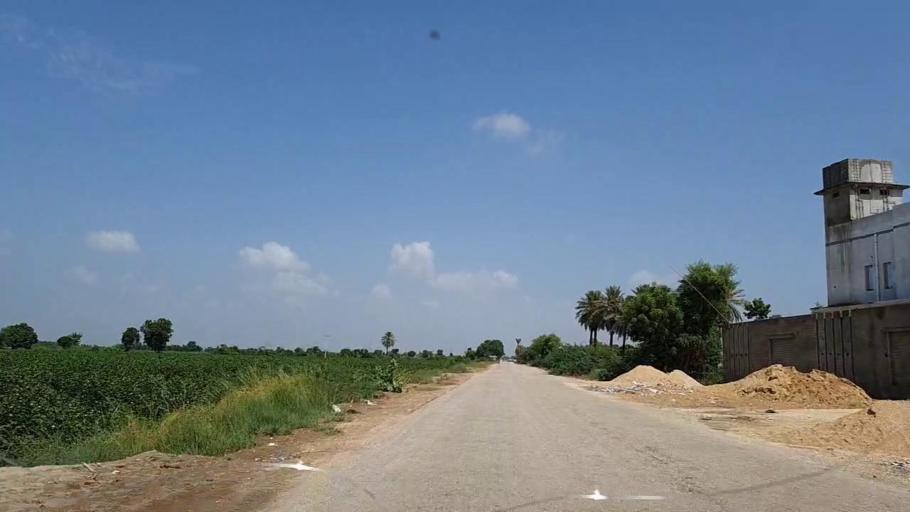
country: PK
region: Sindh
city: Pad Idan
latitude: 26.7892
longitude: 68.2584
